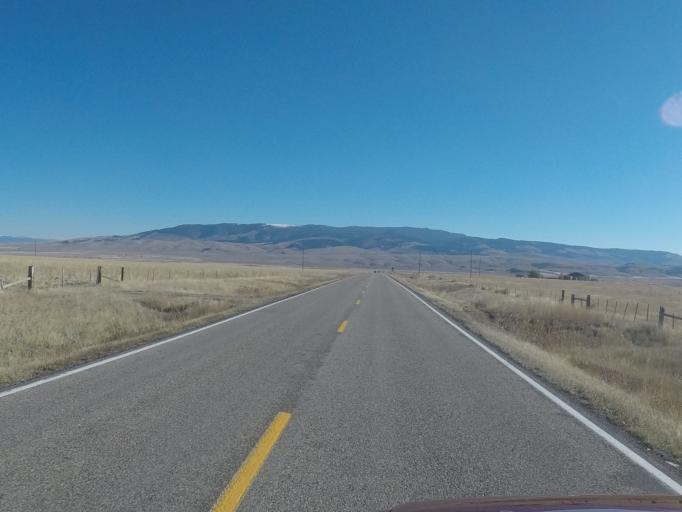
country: US
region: Montana
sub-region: Meagher County
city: White Sulphur Springs
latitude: 46.4021
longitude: -110.9513
